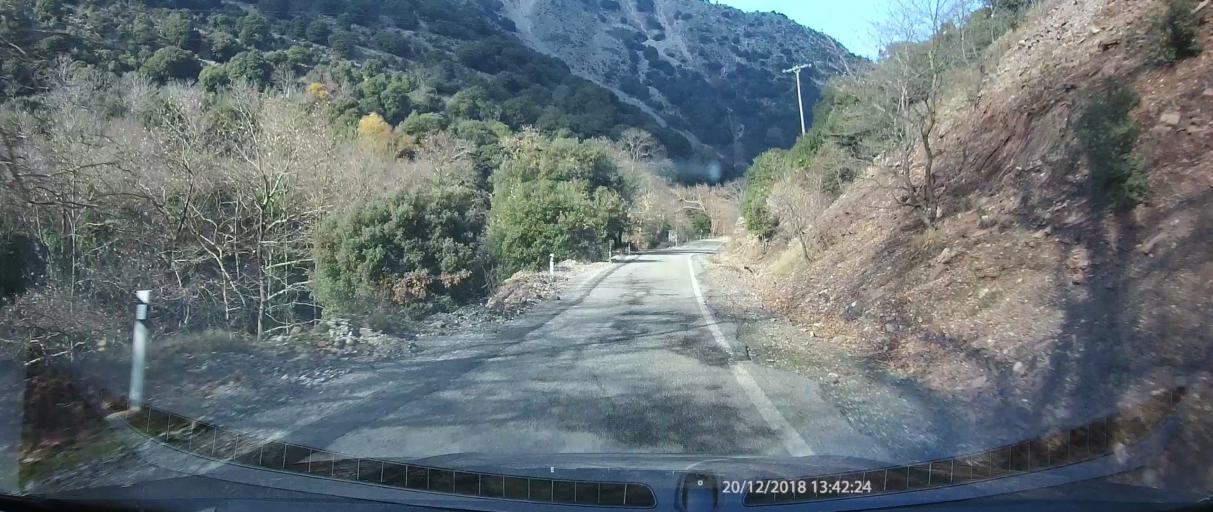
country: GR
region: West Greece
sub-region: Nomos Aitolias kai Akarnanias
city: Thermo
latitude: 38.6536
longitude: 21.6185
